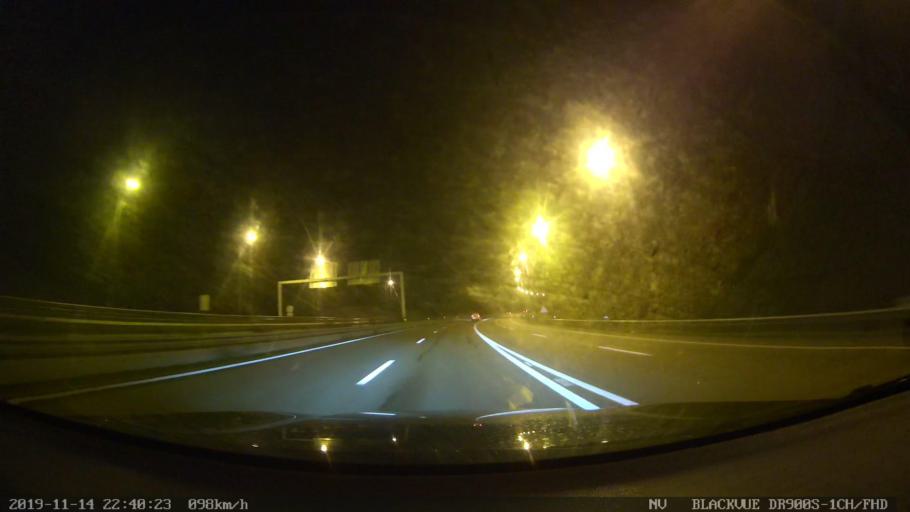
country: PT
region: Porto
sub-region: Felgueiras
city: Margaride
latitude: 41.3270
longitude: -8.2356
